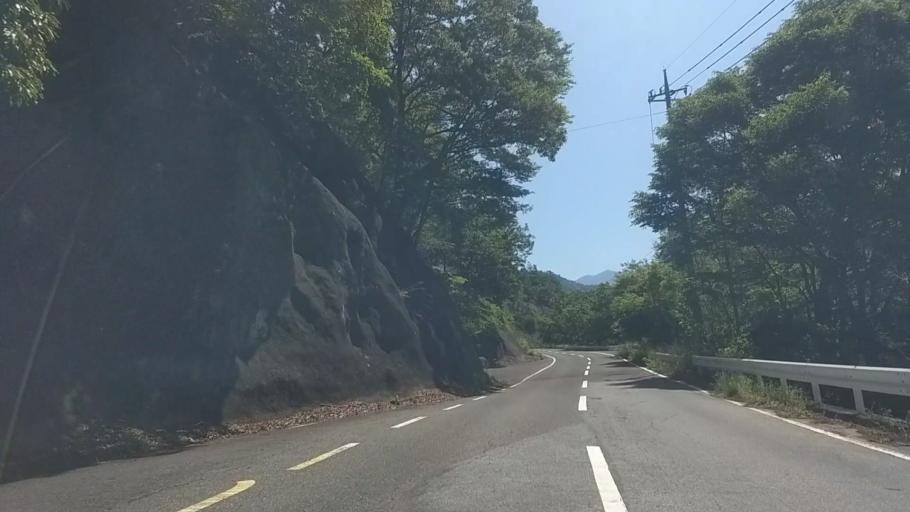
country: JP
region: Yamanashi
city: Ryuo
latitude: 35.5120
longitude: 138.4438
